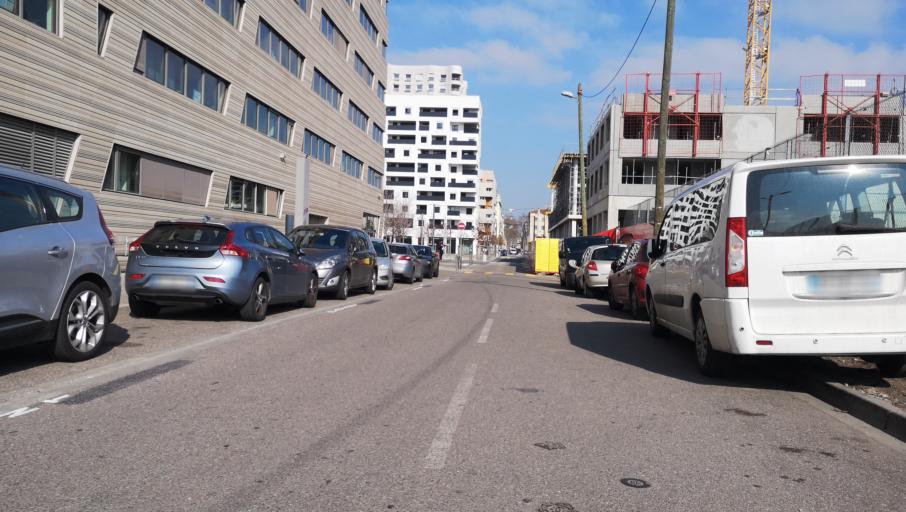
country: FR
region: Rhone-Alpes
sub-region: Departement du Rhone
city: La Mulatiere
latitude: 45.7400
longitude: 4.8200
